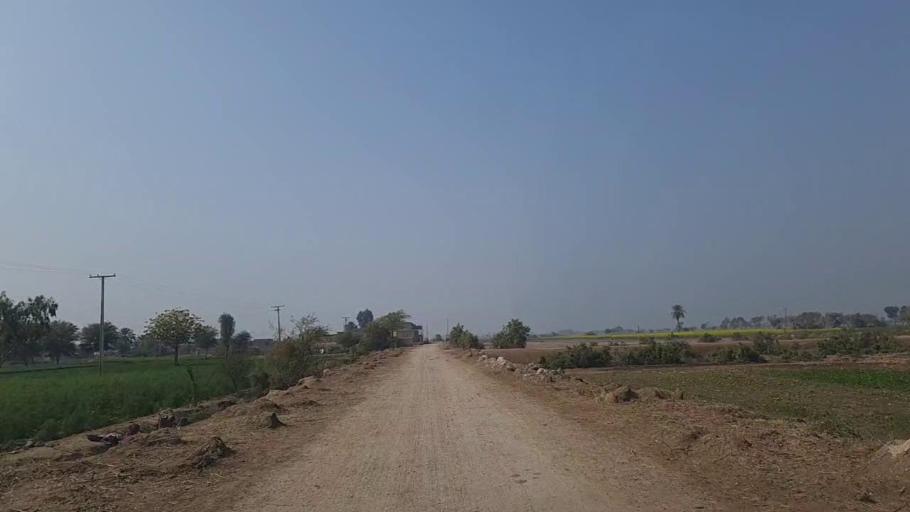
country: PK
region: Sindh
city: Nawabshah
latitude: 26.3601
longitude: 68.4238
